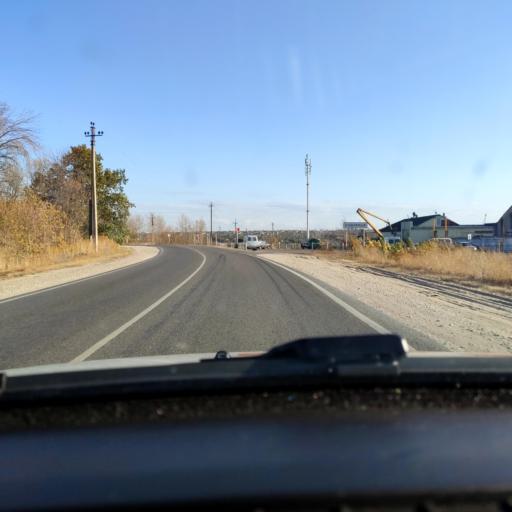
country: RU
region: Voronezj
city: Semiluki
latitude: 51.7239
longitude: 38.9928
